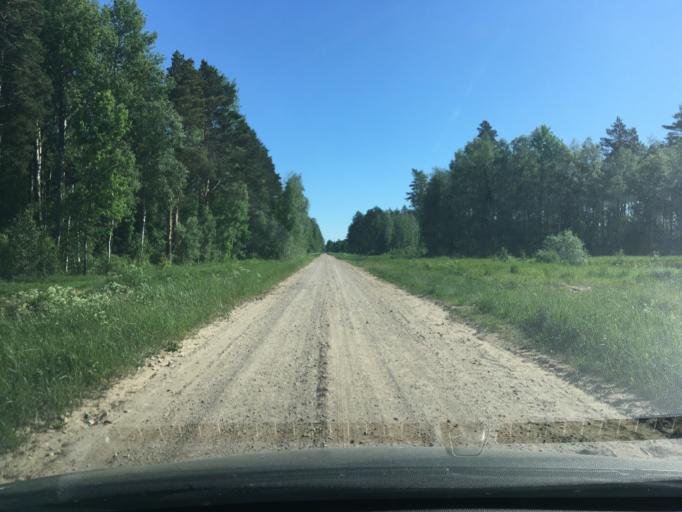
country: EE
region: Laeaene
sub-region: Lihula vald
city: Lihula
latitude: 58.6418
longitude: 23.7696
